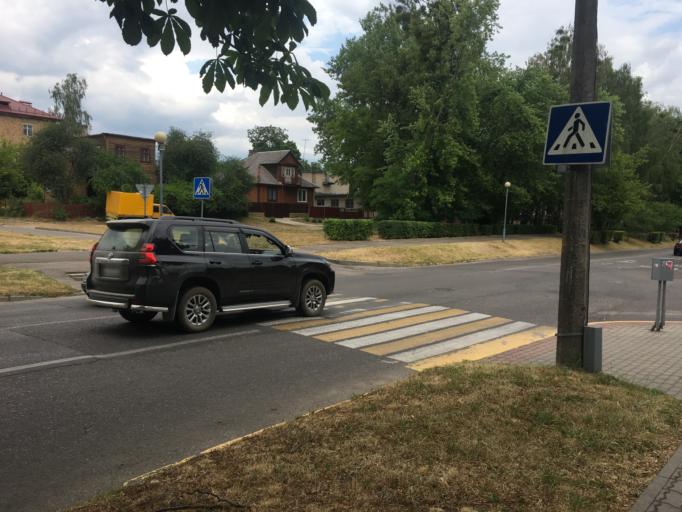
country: BY
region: Grodnenskaya
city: Hrodna
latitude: 53.6893
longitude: 23.8417
